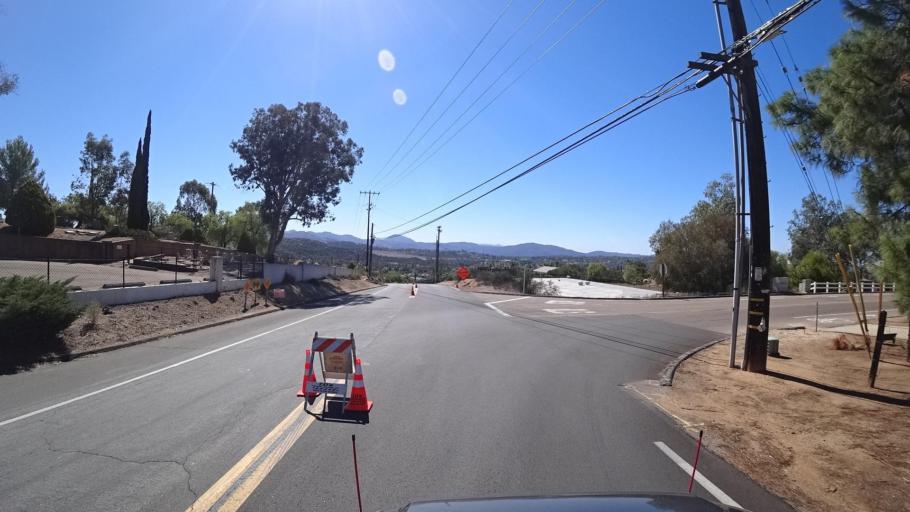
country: US
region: California
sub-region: San Diego County
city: Alpine
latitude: 32.8430
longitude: -116.7681
